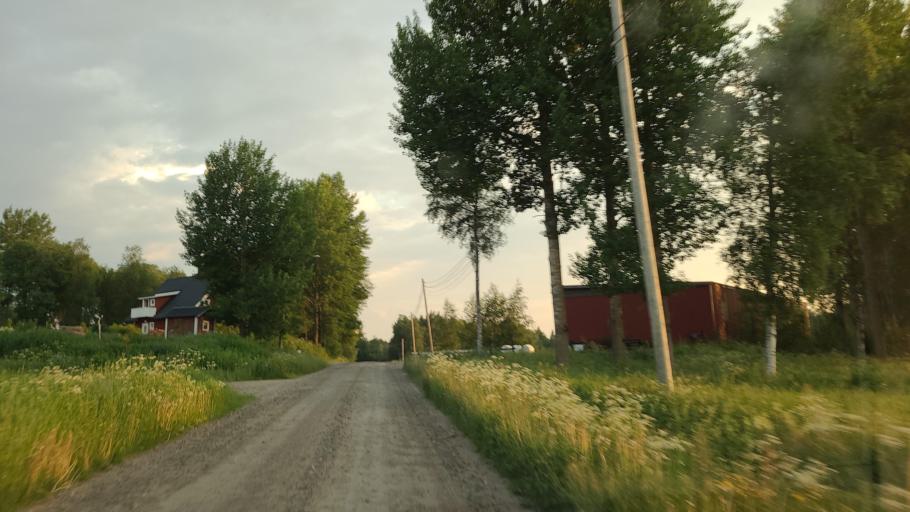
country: SE
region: Vaesterbotten
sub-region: Robertsfors Kommun
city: Robertsfors
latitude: 64.0646
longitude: 20.8671
